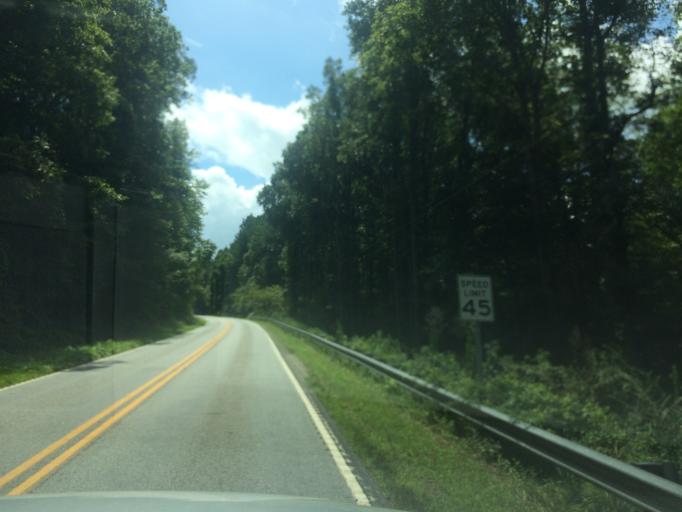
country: US
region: North Carolina
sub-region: Polk County
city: Columbus
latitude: 35.3280
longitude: -82.1849
